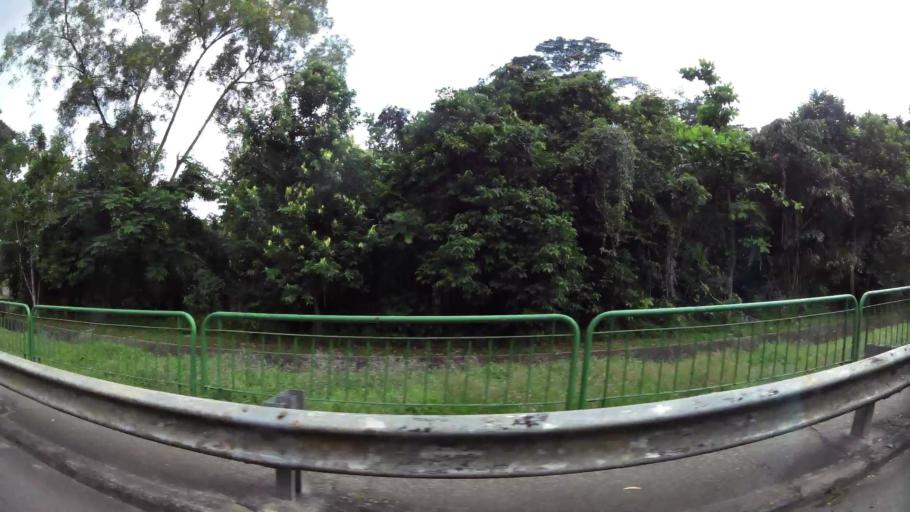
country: MY
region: Johor
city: Kampung Pasir Gudang Baru
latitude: 1.4571
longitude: 103.8215
